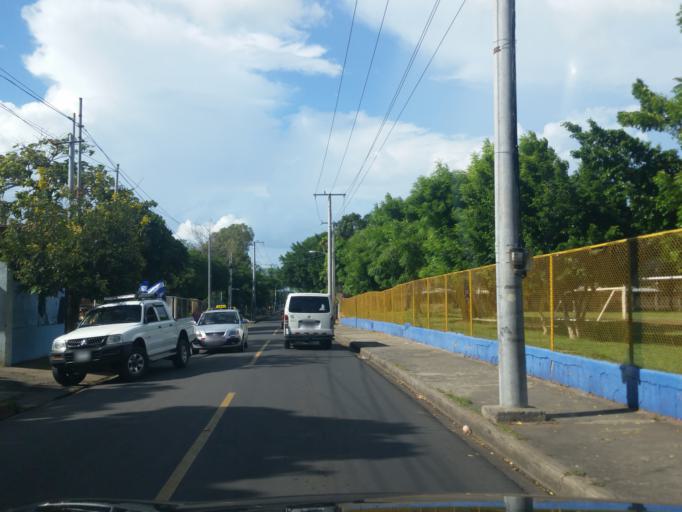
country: NI
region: Managua
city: Managua
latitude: 12.1482
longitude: -86.2682
